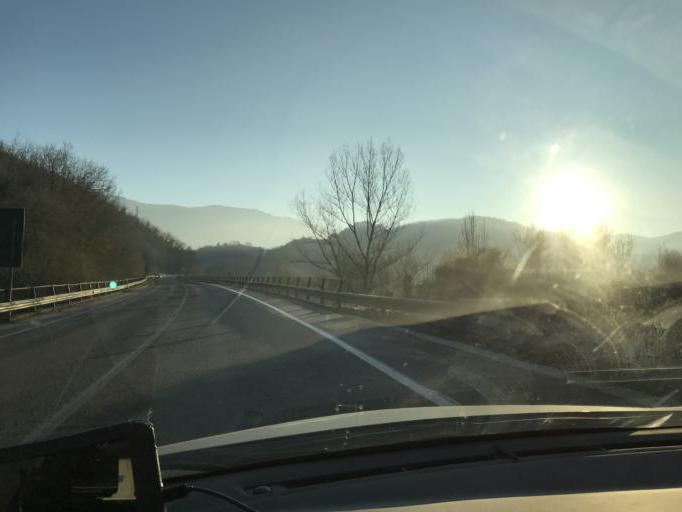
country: IT
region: Latium
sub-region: Provincia di Rieti
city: Concerviano
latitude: 42.3319
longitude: 12.9833
